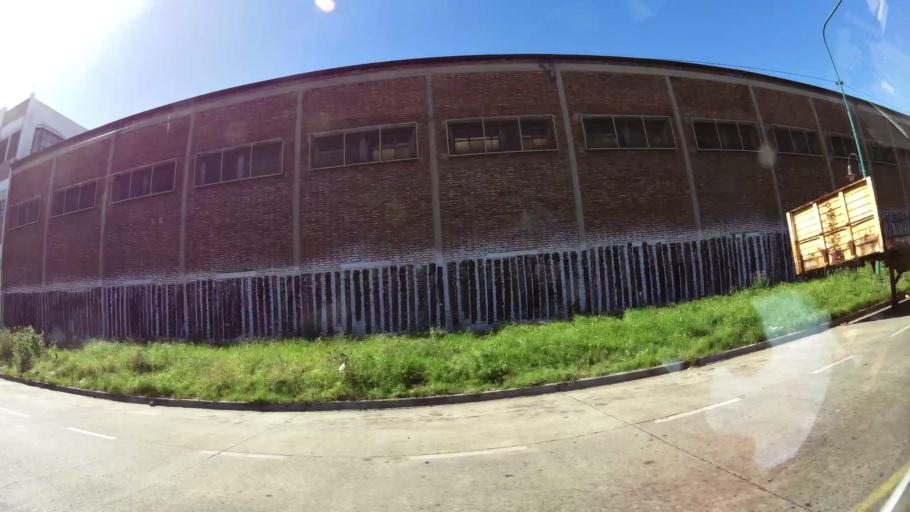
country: AR
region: Buenos Aires
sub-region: Partido de General San Martin
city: General San Martin
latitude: -34.5419
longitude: -58.5281
